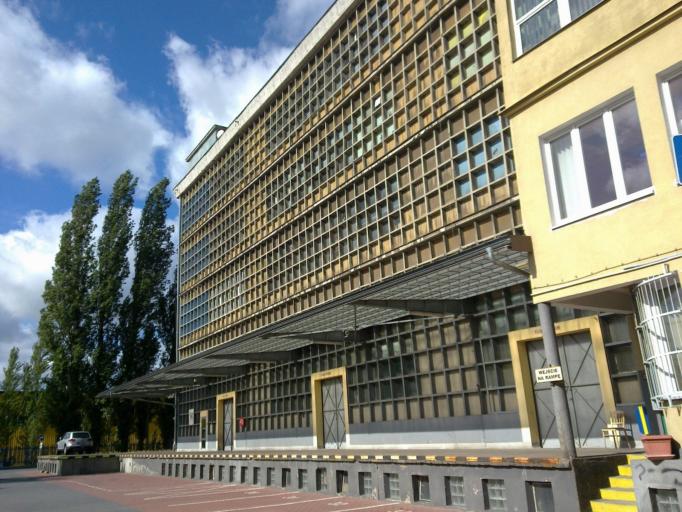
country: PL
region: Pomeranian Voivodeship
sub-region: Gdynia
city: Gdynia
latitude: 54.5243
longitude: 18.5405
